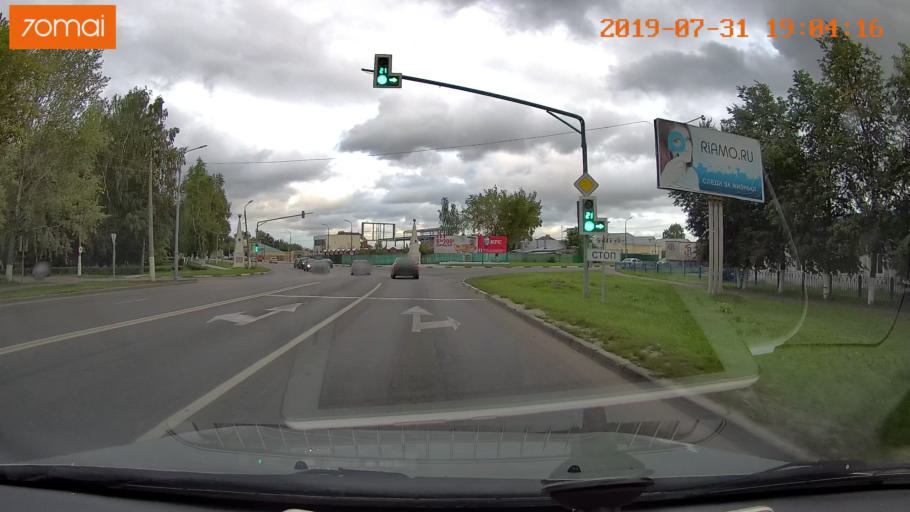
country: RU
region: Moskovskaya
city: Raduzhnyy
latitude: 55.1097
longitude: 38.7401
